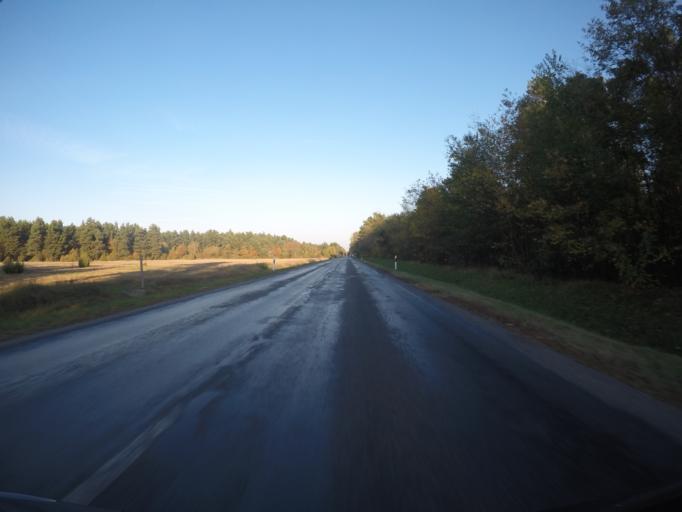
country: HU
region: Somogy
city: Barcs
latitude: 45.9775
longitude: 17.5654
